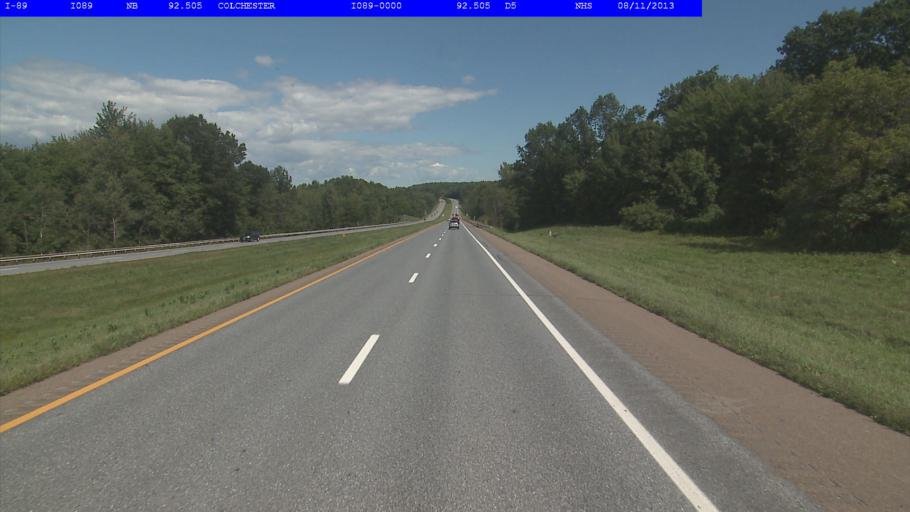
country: US
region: Vermont
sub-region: Chittenden County
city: Winooski
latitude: 44.5168
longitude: -73.1919
